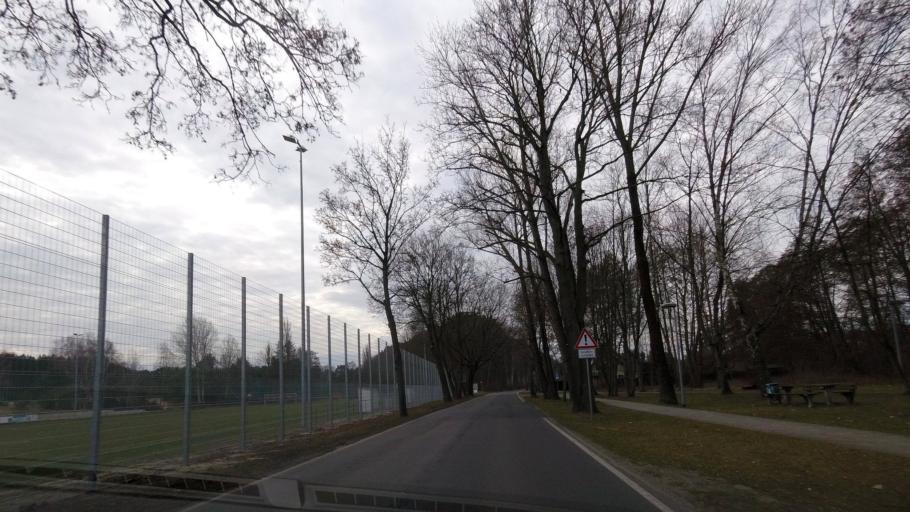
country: DE
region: Berlin
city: Schmockwitz
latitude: 52.3685
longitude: 13.7006
